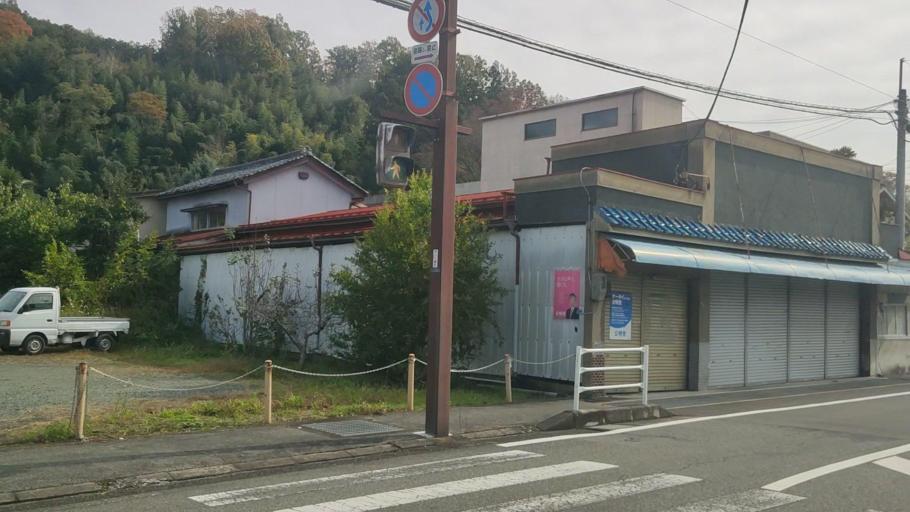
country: JP
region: Yamanashi
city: Ryuo
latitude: 35.5397
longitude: 138.4715
